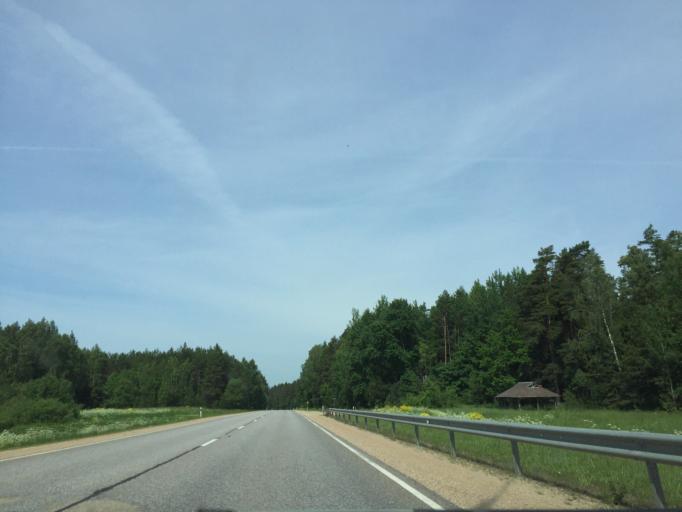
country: LV
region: Koknese
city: Koknese
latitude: 56.5956
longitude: 25.5379
